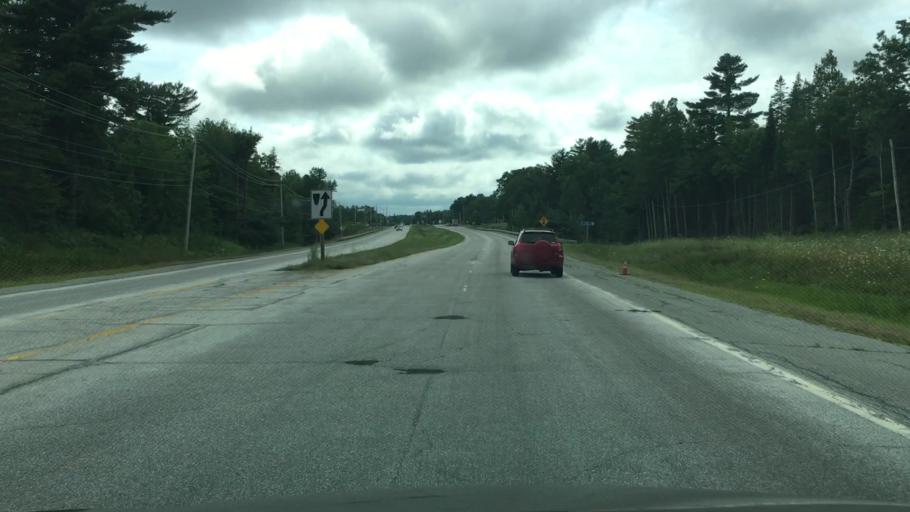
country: US
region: Maine
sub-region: Penobscot County
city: Hampden
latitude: 44.7570
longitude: -68.8338
